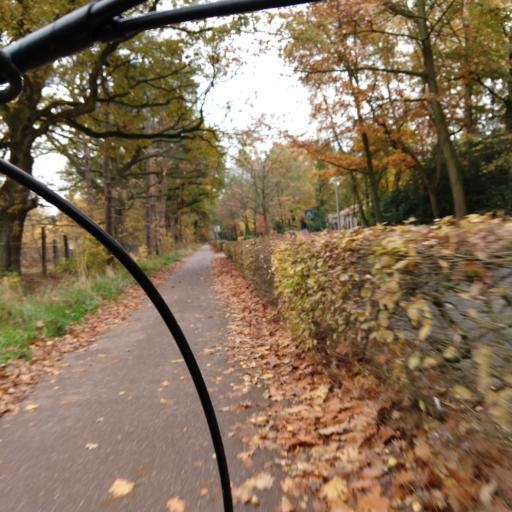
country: BE
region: Flanders
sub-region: Provincie Antwerpen
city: Kapellen
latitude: 51.3621
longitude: 4.4227
